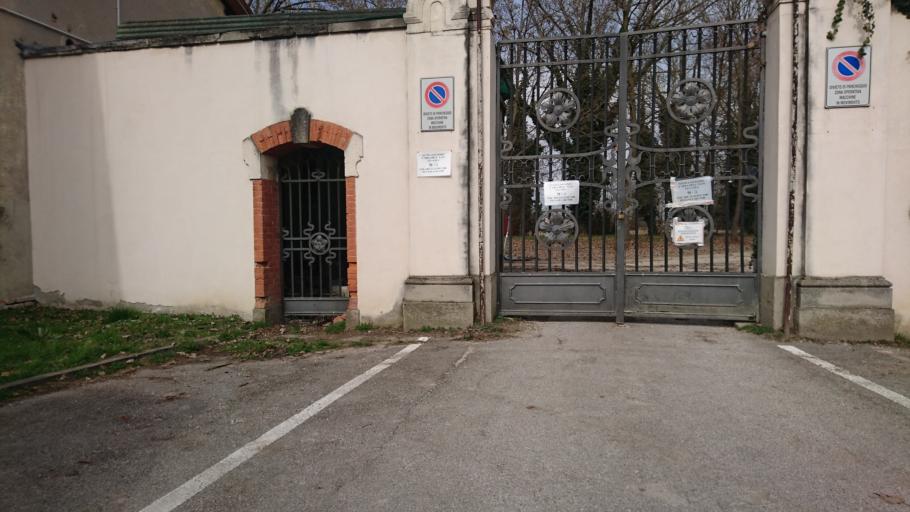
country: IT
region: Veneto
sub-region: Provincia di Padova
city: Caselle
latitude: 45.4009
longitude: 11.8424
